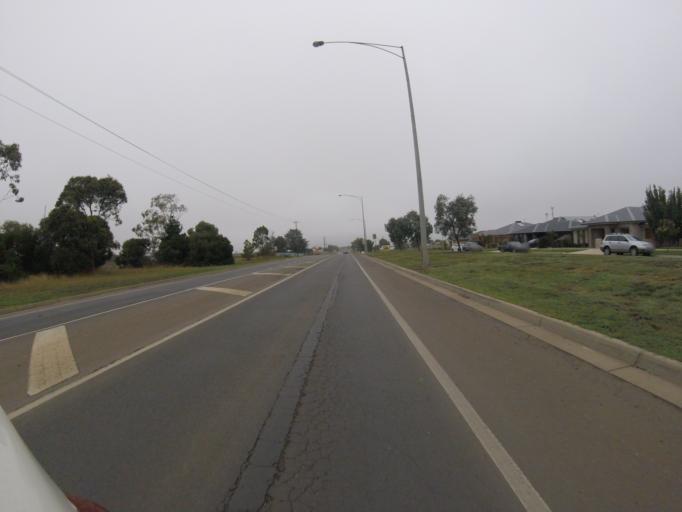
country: AU
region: Victoria
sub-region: Ballarat North
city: Newington
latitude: -37.5606
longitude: 143.8121
